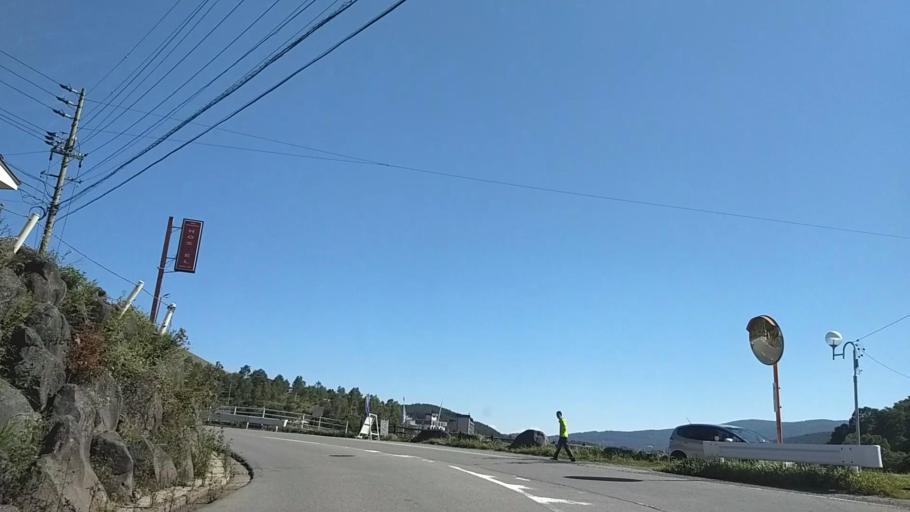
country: JP
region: Nagano
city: Chino
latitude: 36.1015
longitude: 138.2288
